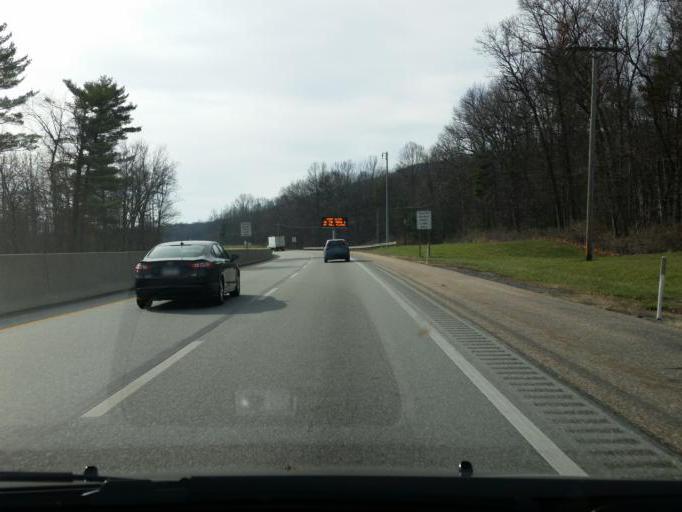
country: US
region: Pennsylvania
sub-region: Franklin County
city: Doylestown
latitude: 40.0922
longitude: -77.8233
